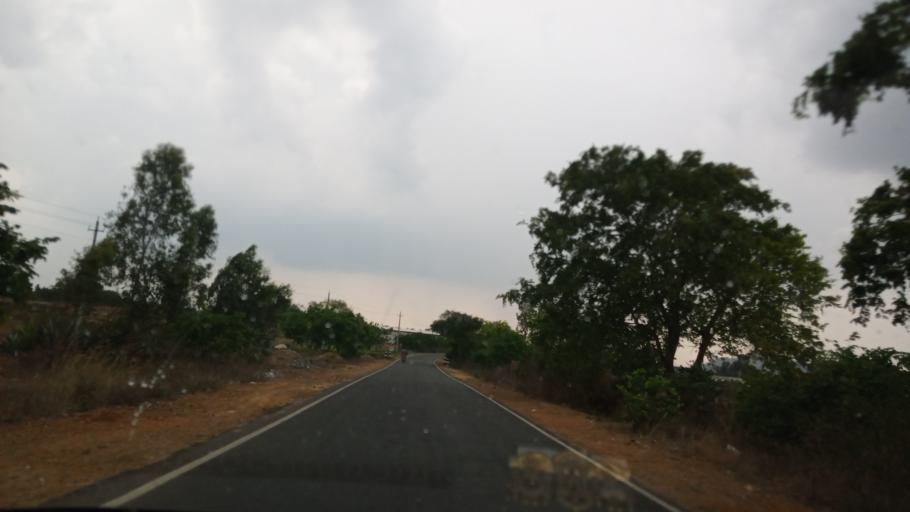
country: IN
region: Karnataka
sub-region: Kolar
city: Mulbagal
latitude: 13.1331
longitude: 78.3566
